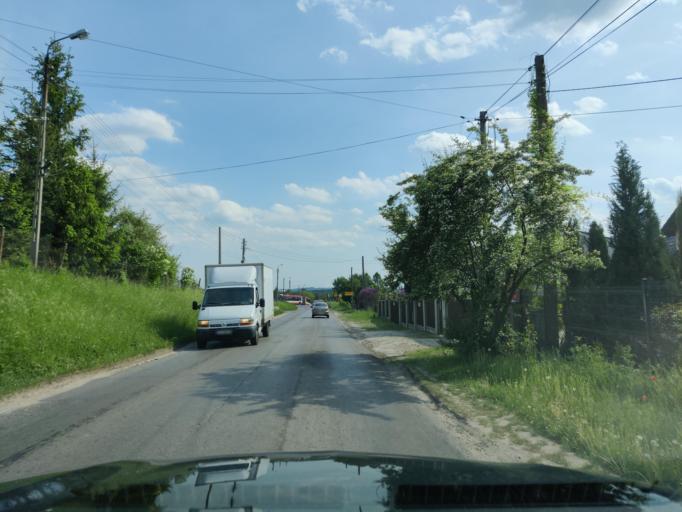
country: PL
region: Silesian Voivodeship
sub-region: Dabrowa Gornicza
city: Dabrowa Gornicza
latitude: 50.3871
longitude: 19.2421
